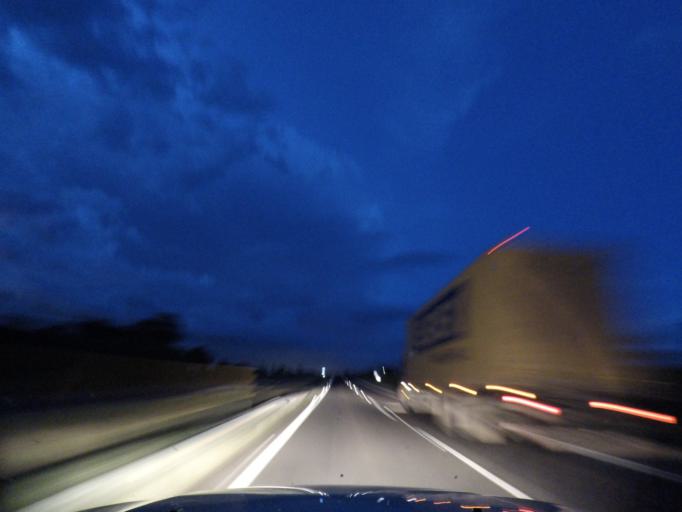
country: BR
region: Minas Gerais
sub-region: Uberlandia
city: Uberlandia
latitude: -19.2163
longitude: -48.1469
